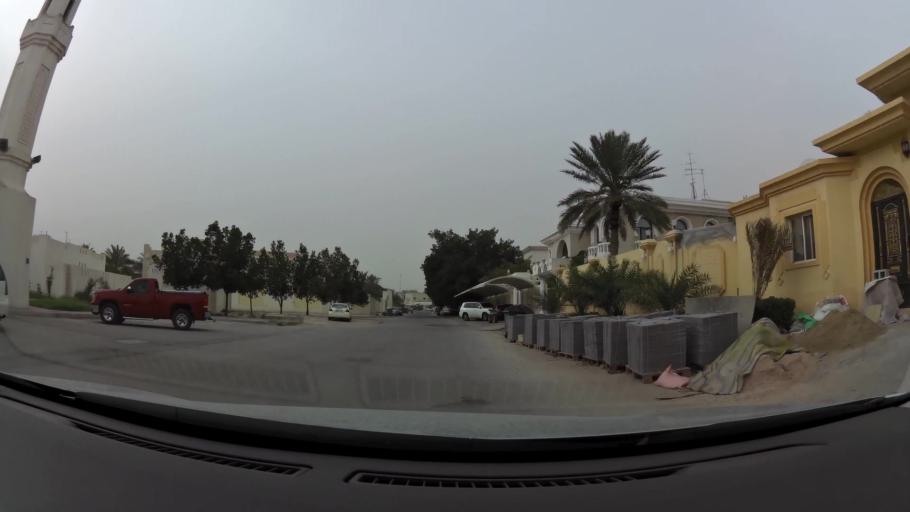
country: QA
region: Baladiyat ad Dawhah
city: Doha
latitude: 25.2571
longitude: 51.4935
